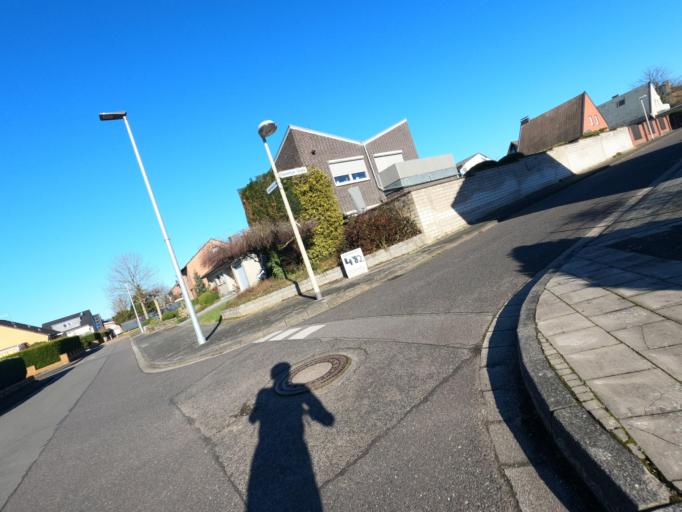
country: DE
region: North Rhine-Westphalia
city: Huckelhoven
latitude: 51.0509
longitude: 6.2322
